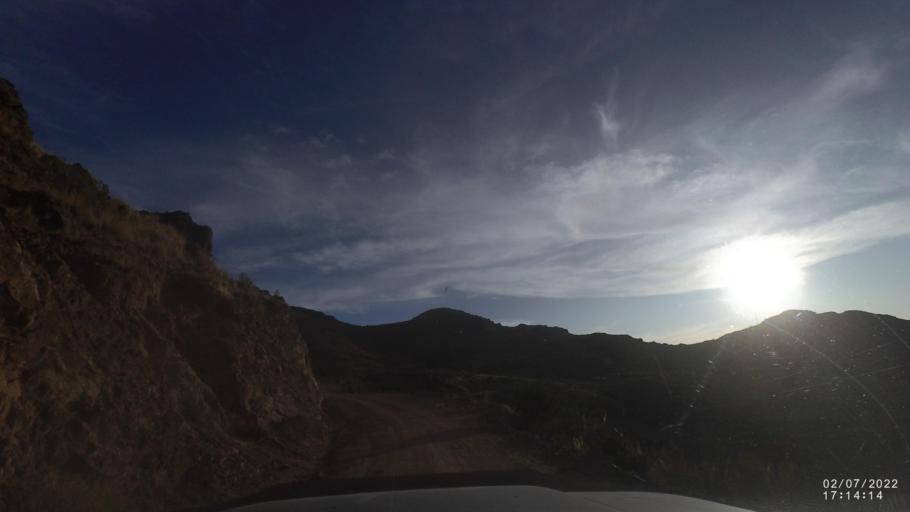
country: BO
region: Cochabamba
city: Irpa Irpa
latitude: -17.8786
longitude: -66.5795
